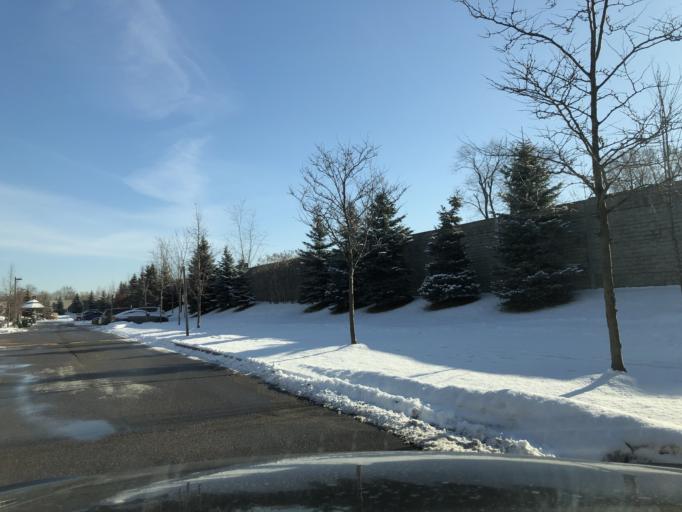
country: CA
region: Ontario
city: Etobicoke
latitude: 43.7073
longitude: -79.5314
